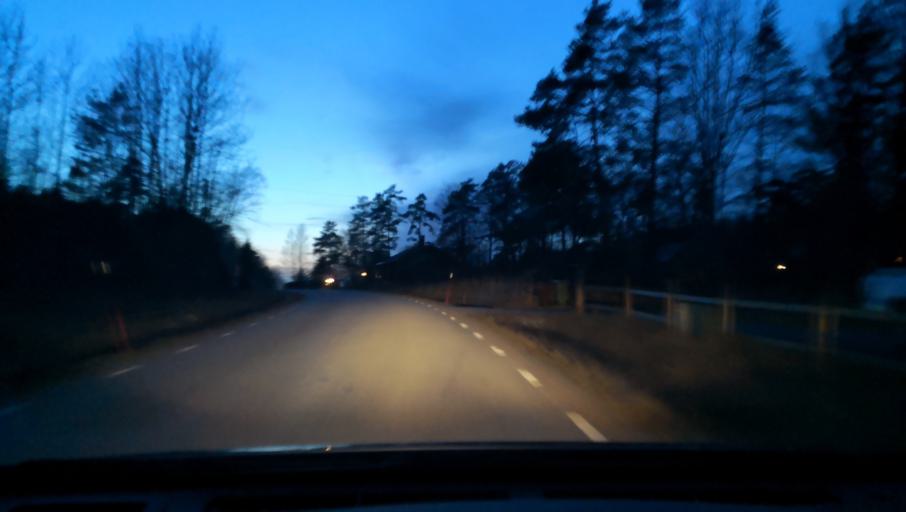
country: SE
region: Uppsala
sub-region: Enkopings Kommun
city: Grillby
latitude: 59.6069
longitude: 17.2833
